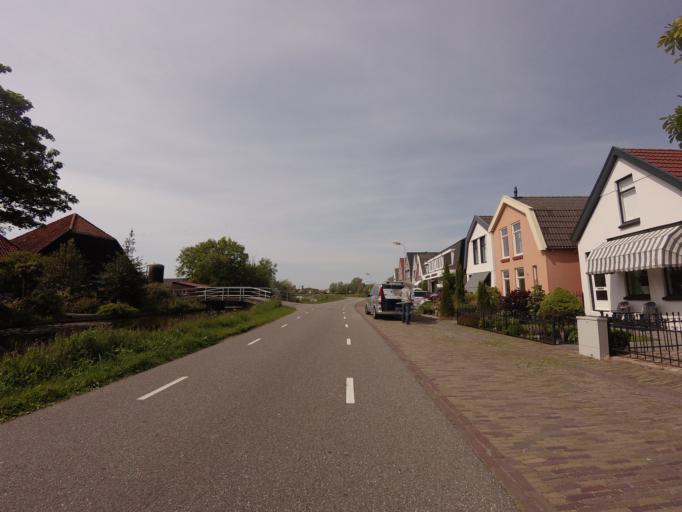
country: NL
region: North Holland
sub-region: Gemeente Uitgeest
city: Uitgeest
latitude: 52.5102
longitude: 4.7698
